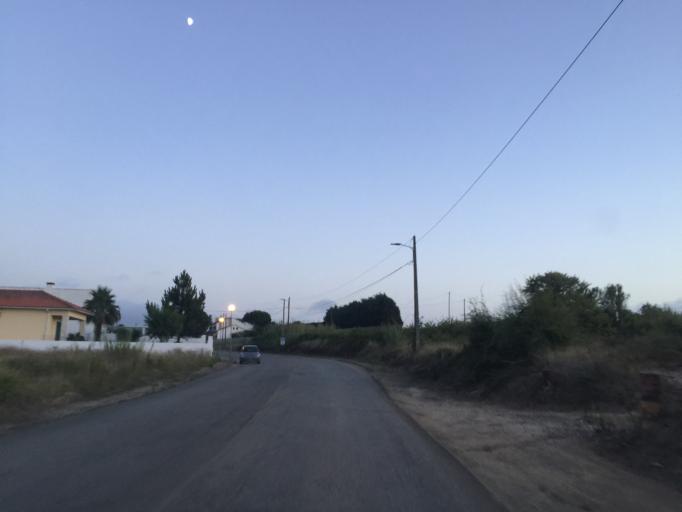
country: PT
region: Leiria
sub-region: Bombarral
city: Bombarral
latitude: 39.2717
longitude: -9.1659
